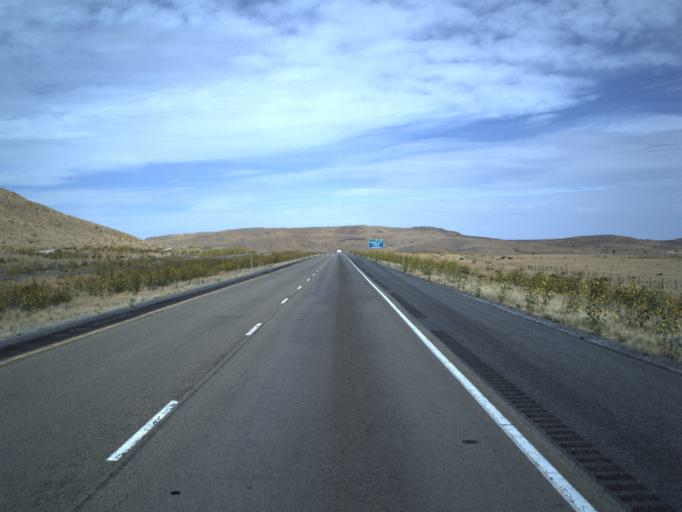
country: US
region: Utah
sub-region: Tooele County
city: Grantsville
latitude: 40.8165
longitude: -112.8792
